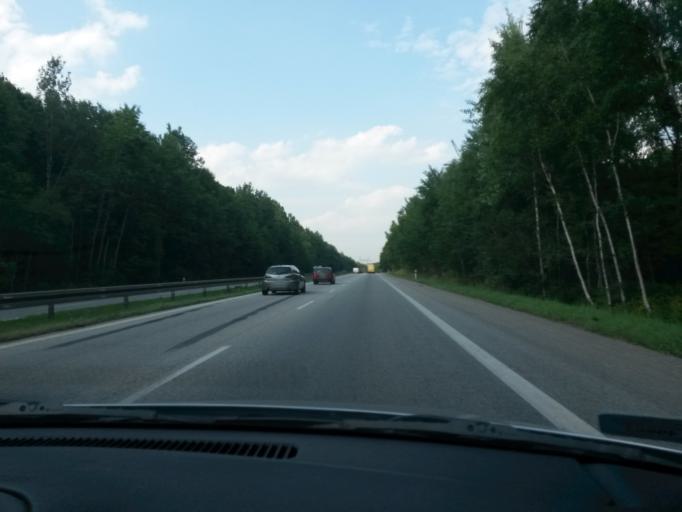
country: PL
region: Silesian Voivodeship
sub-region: Dabrowa Gornicza
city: Dabrowa Gornicza
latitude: 50.3025
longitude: 19.2234
